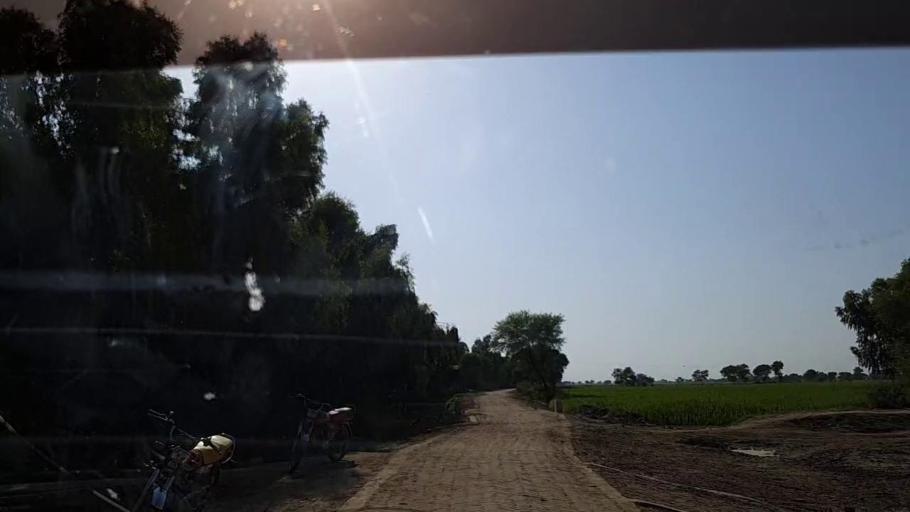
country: PK
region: Sindh
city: Tangwani
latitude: 28.2148
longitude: 68.9775
